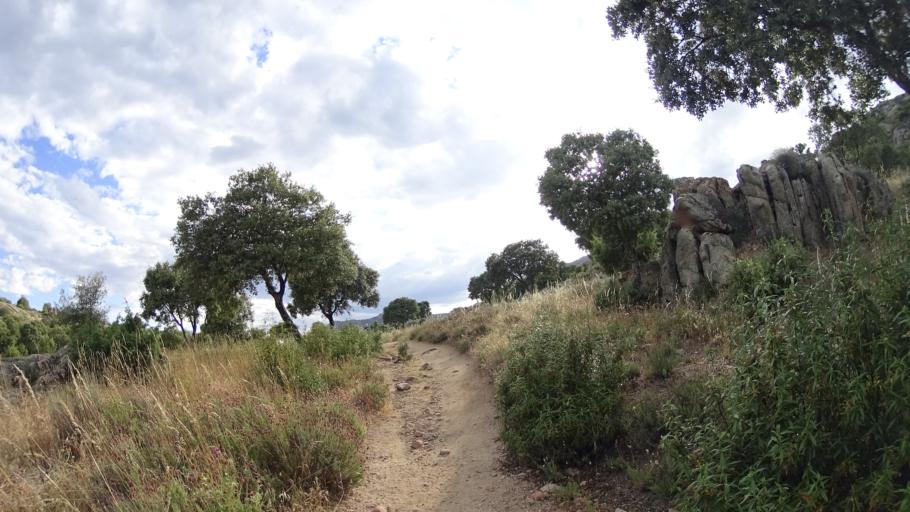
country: ES
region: Madrid
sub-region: Provincia de Madrid
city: Hoyo de Manzanares
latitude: 40.6342
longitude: -3.8989
